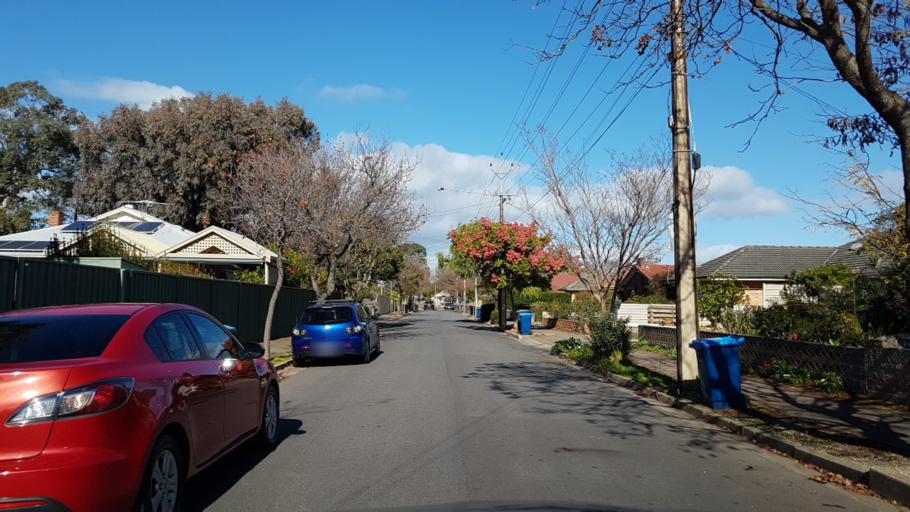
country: AU
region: South Australia
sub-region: Mitcham
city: Clarence Gardens
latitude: -34.9652
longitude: 138.5782
